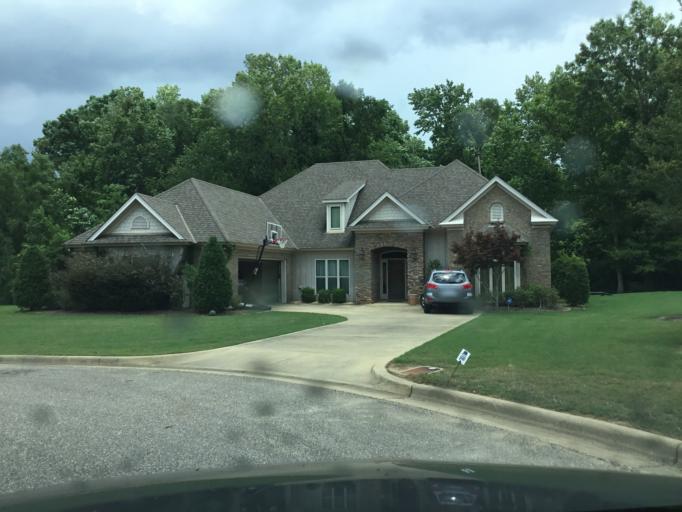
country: US
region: Alabama
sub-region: Montgomery County
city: Pike Road
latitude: 32.3431
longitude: -86.0855
